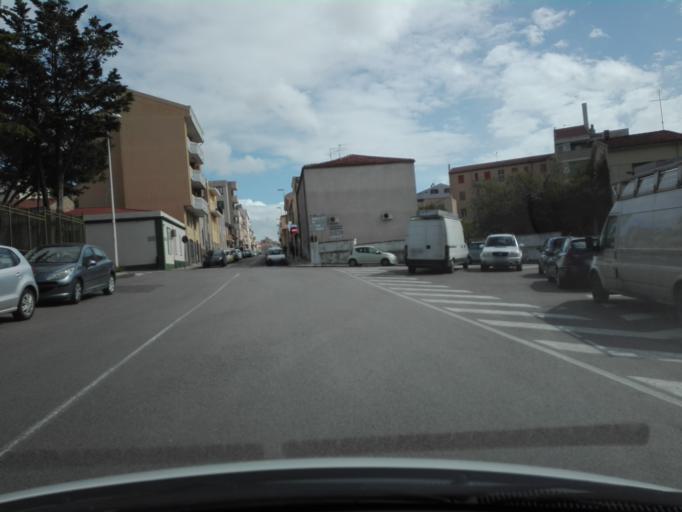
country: IT
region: Sardinia
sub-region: Provincia di Sassari
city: Sassari
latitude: 40.7356
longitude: 8.5644
